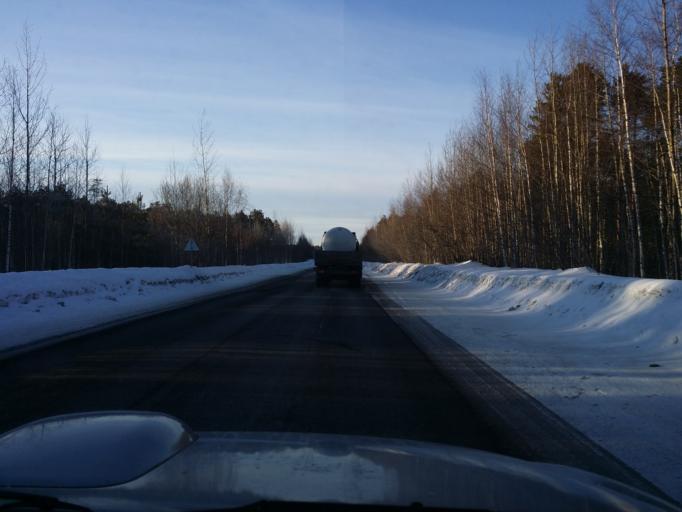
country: RU
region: Khanty-Mansiyskiy Avtonomnyy Okrug
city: Izluchinsk
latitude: 60.9397
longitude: 76.8609
